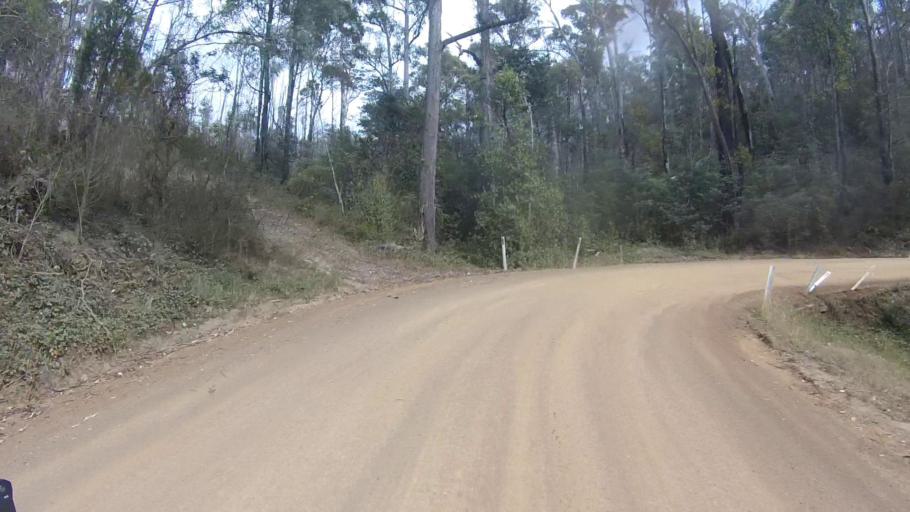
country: AU
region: Tasmania
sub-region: Sorell
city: Sorell
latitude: -42.7337
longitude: 147.7599
